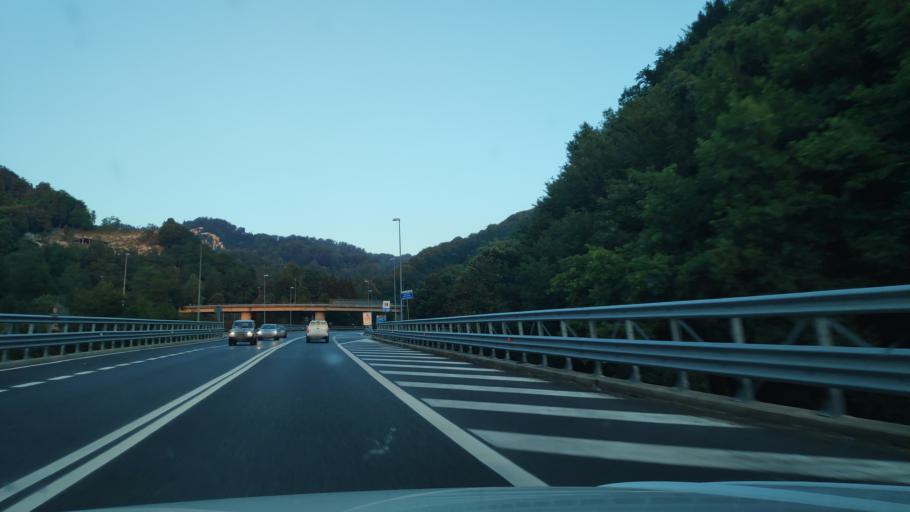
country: IT
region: Calabria
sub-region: Provincia di Reggio Calabria
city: Amato
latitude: 38.4033
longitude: 16.1592
